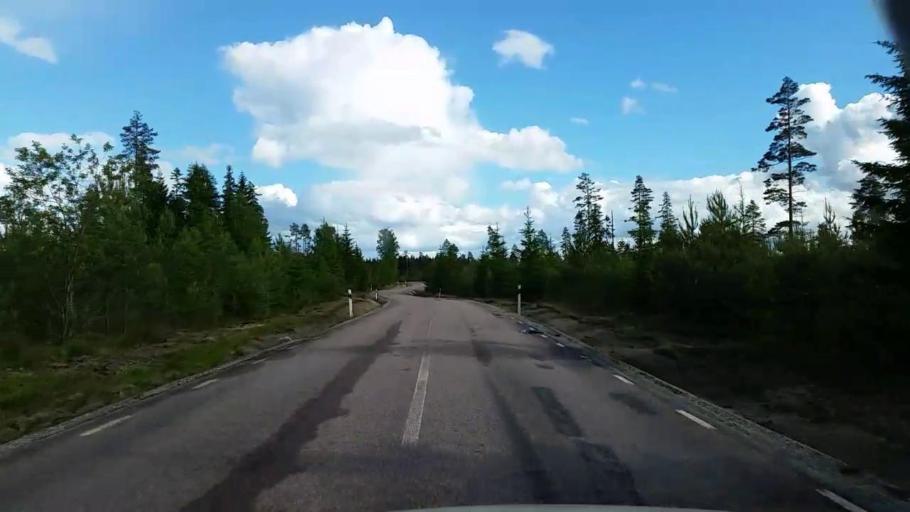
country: SE
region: Vaestmanland
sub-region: Fagersta Kommun
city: Fagersta
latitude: 59.8915
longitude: 15.8239
